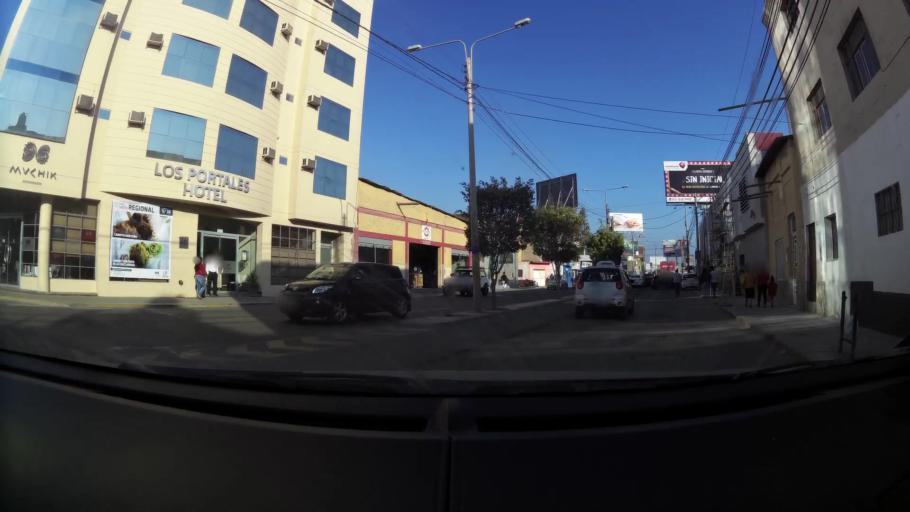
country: PE
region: Lambayeque
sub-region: Provincia de Chiclayo
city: Chiclayo
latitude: -6.7748
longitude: -79.8359
